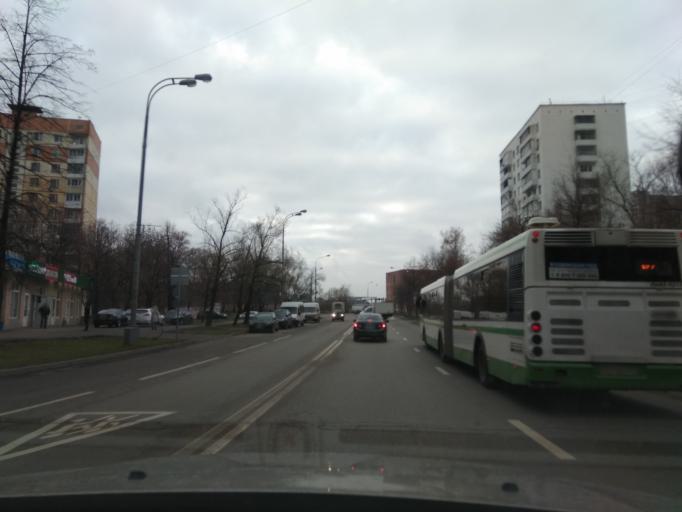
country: RU
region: Moscow
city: Likhobory
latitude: 55.8565
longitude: 37.5669
